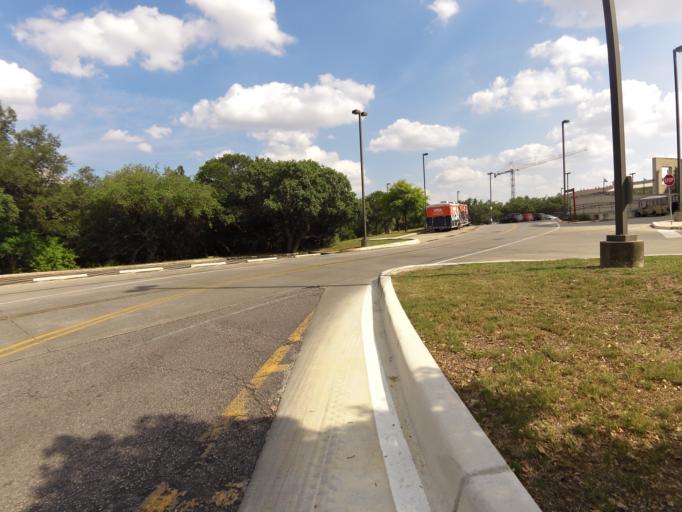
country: US
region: Texas
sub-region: Bexar County
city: Shavano Park
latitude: 29.5852
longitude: -98.6159
